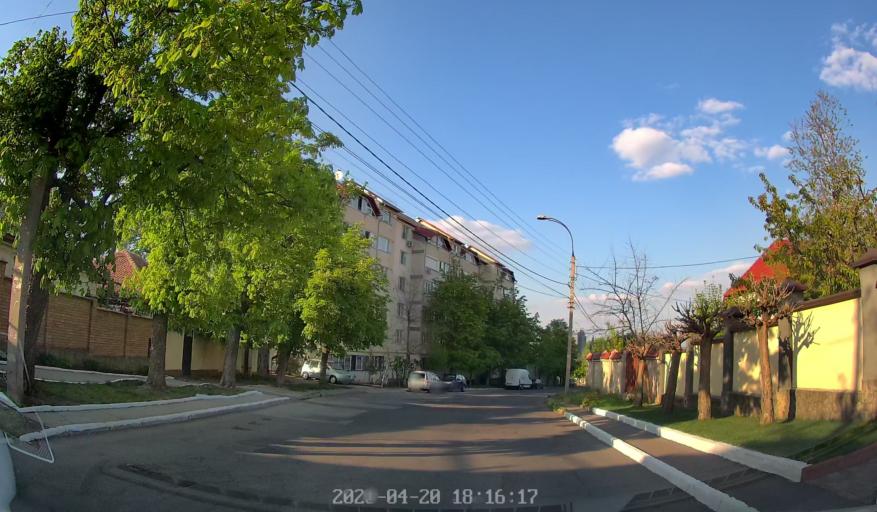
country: MD
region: Chisinau
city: Chisinau
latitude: 47.0006
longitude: 28.8337
